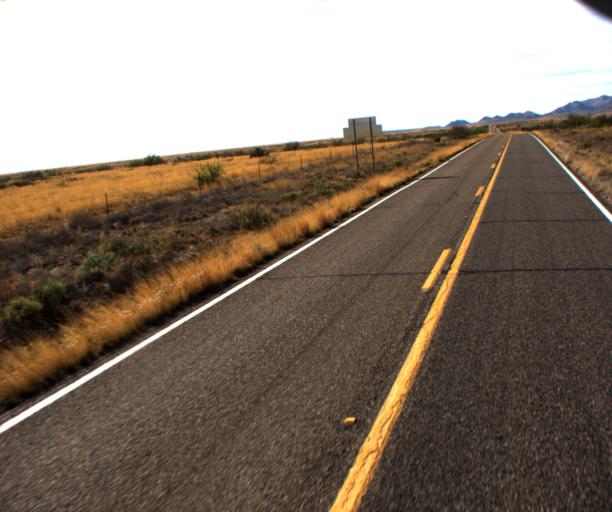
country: US
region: Arizona
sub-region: Cochise County
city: Willcox
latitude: 32.0929
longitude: -109.5336
